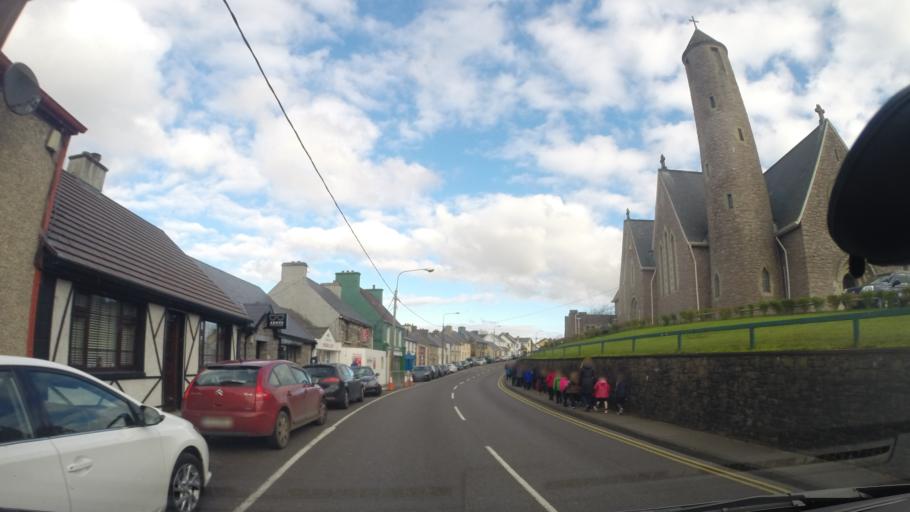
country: IE
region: Ulster
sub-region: County Donegal
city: Donegal
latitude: 54.6541
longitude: -8.1072
